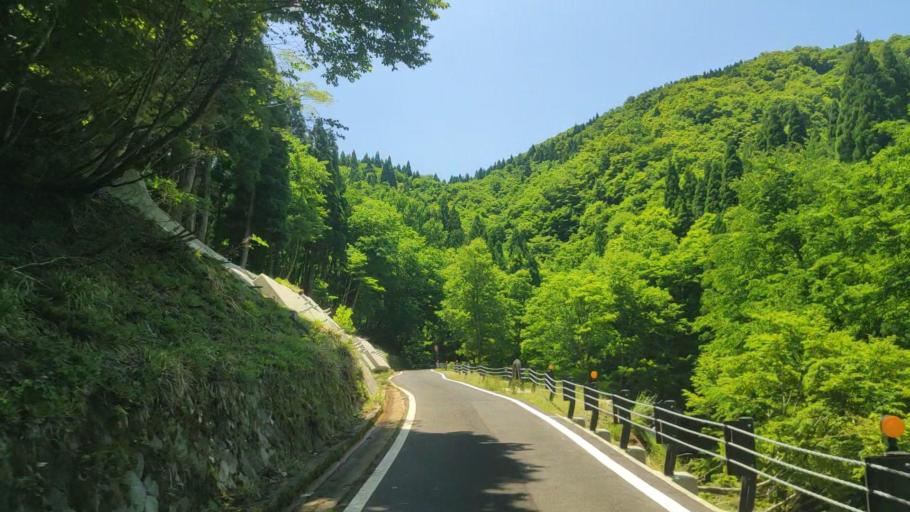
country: JP
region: Tottori
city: Tottori
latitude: 35.3725
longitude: 134.4910
